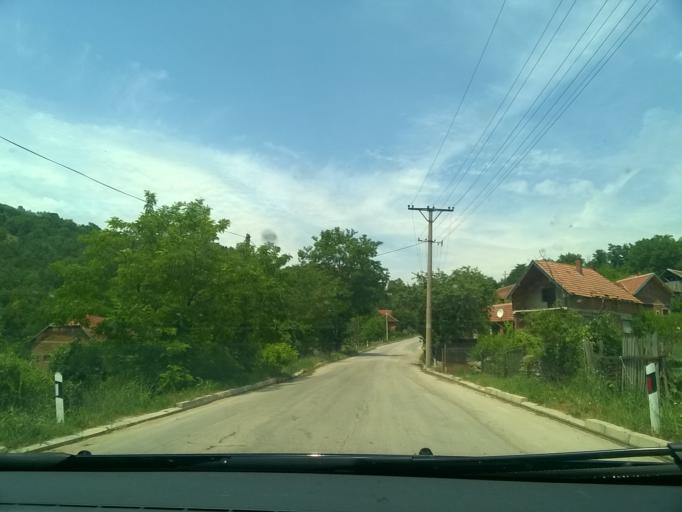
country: RS
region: Central Serbia
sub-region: Nisavski Okrug
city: Aleksinac
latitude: 43.6371
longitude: 21.7154
